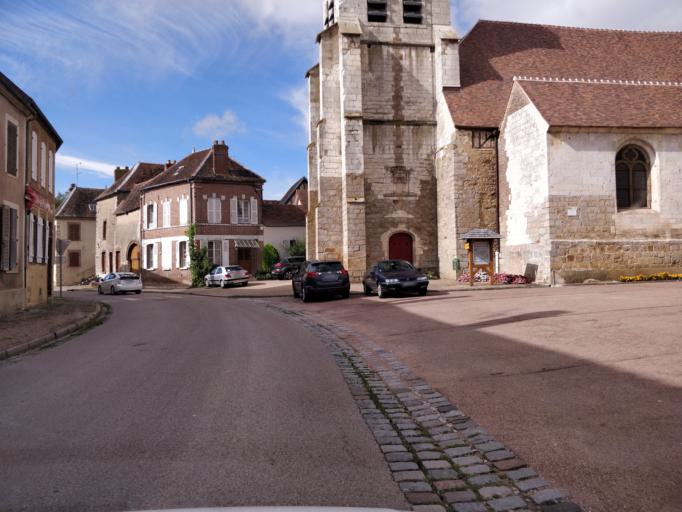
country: FR
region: Champagne-Ardenne
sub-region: Departement de l'Aube
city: Aix-en-Othe
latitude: 48.2084
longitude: 3.6308
